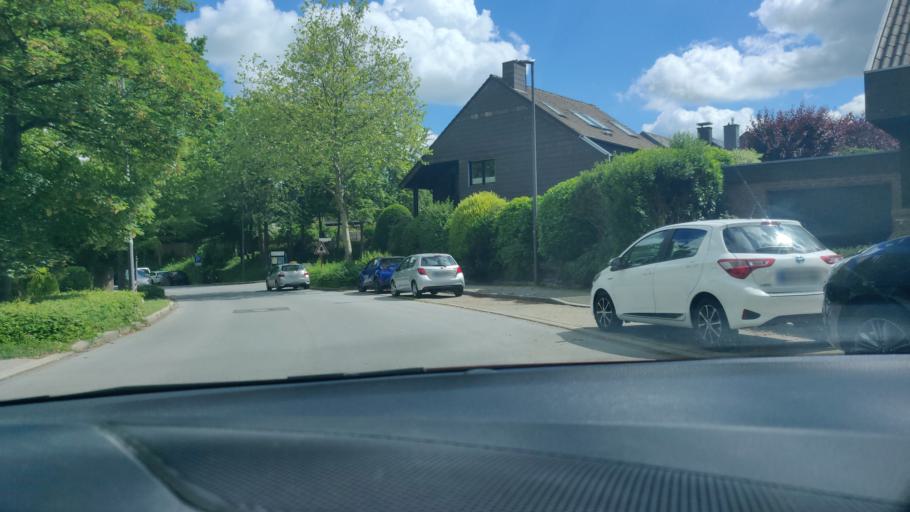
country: DE
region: North Rhine-Westphalia
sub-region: Regierungsbezirk Dusseldorf
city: Heiligenhaus
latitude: 51.3236
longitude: 6.9863
